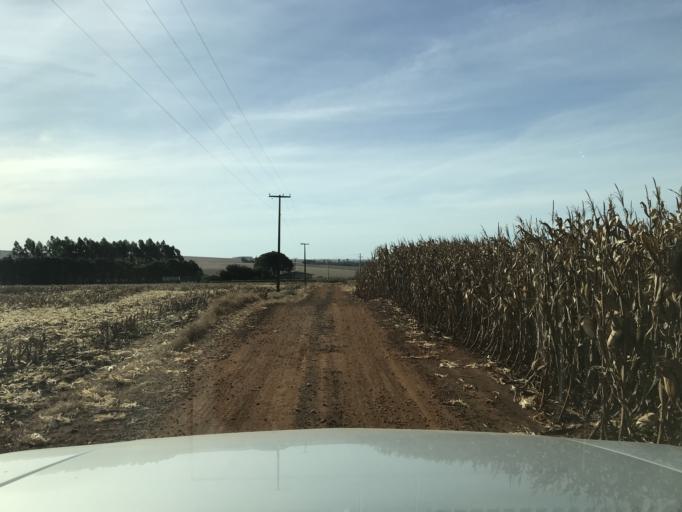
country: BR
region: Parana
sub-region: Palotina
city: Palotina
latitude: -24.2603
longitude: -53.7486
